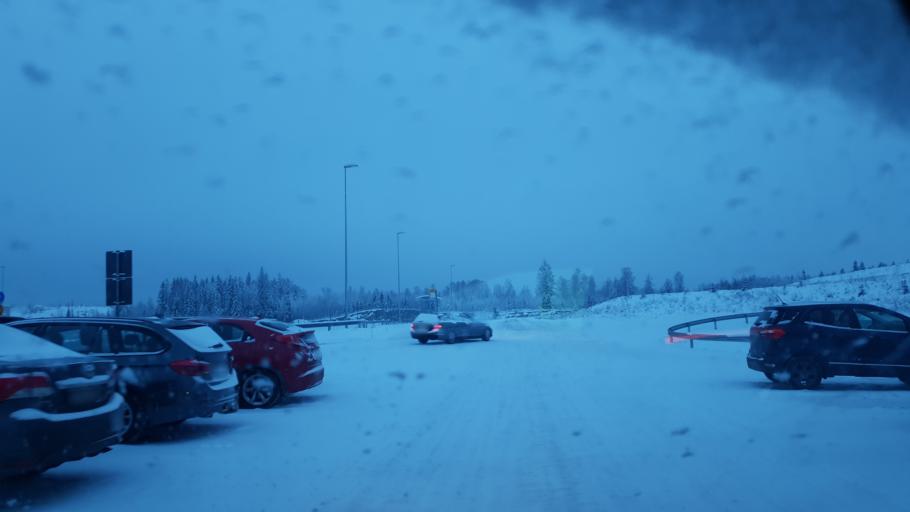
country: FI
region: Uusimaa
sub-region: Helsinki
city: Kerava
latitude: 60.3762
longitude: 25.1519
